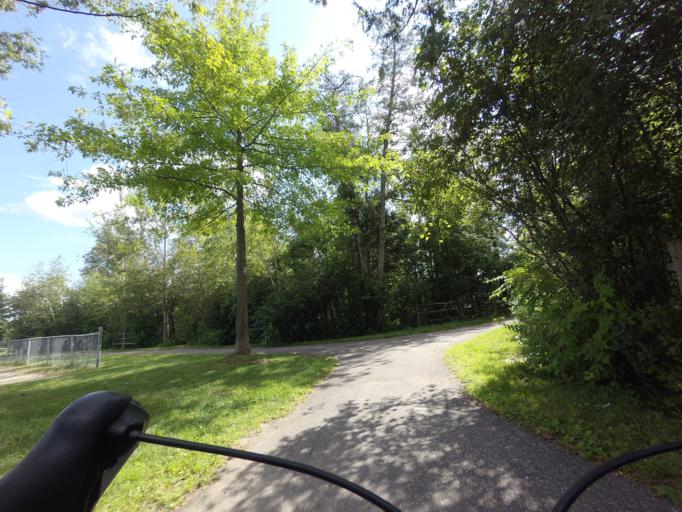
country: CA
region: Ontario
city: Bells Corners
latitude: 45.3001
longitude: -75.8556
